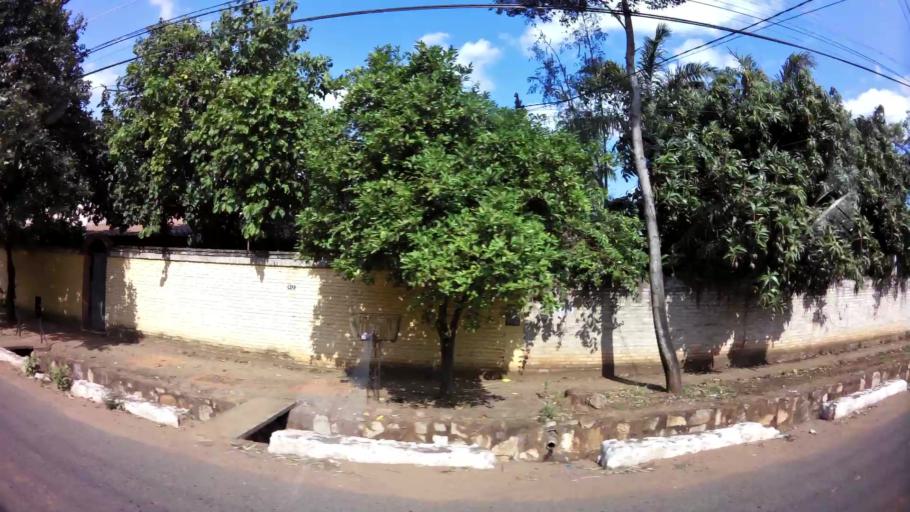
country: PY
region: Central
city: Fernando de la Mora
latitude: -25.3315
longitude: -57.5307
